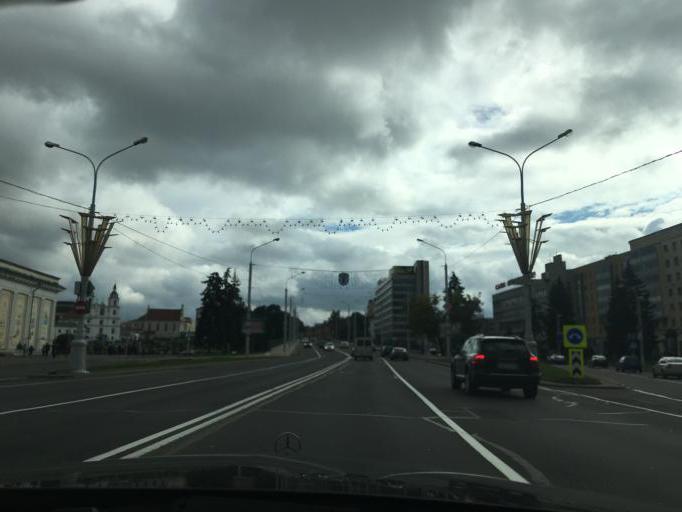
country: BY
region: Minsk
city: Minsk
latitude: 53.9073
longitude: 27.5515
